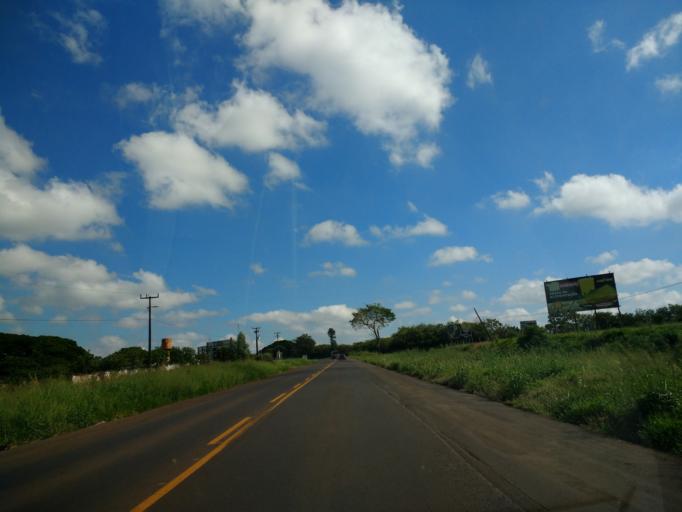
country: BR
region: Parana
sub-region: Umuarama
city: Umuarama
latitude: -23.8290
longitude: -53.3497
